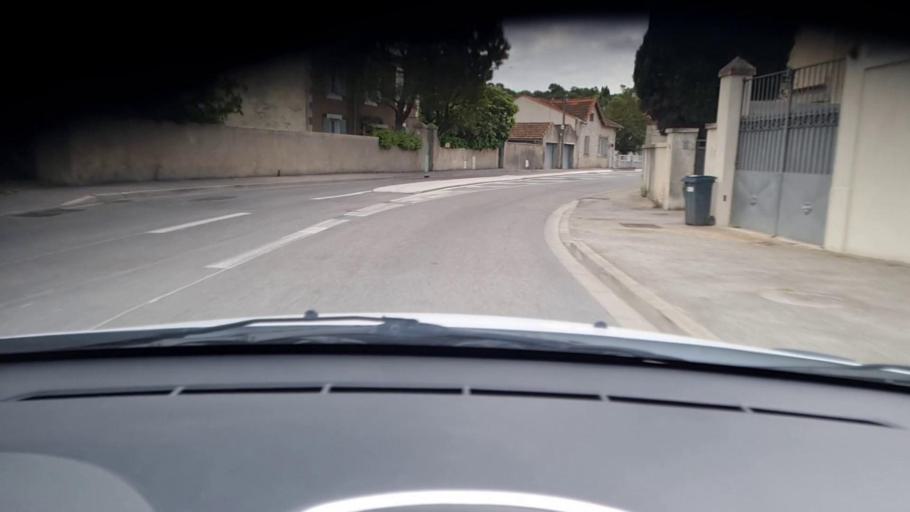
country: FR
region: Languedoc-Roussillon
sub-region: Departement du Gard
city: Nimes
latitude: 43.8552
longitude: 4.3797
